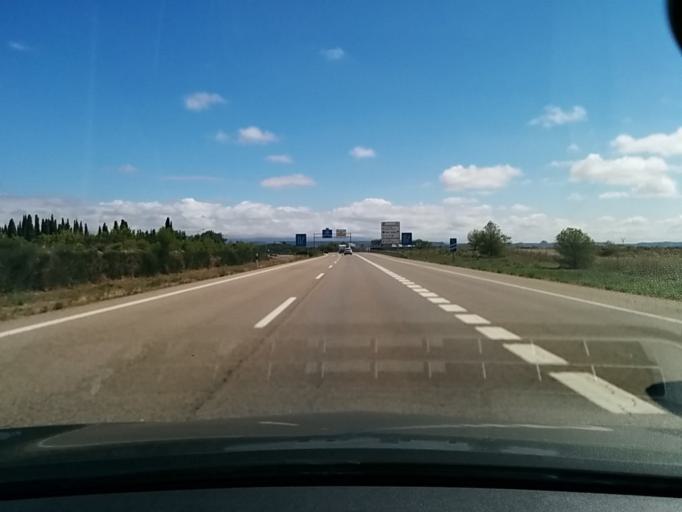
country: ES
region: Aragon
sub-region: Provincia de Huesca
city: Huesca
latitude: 42.1200
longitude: -0.4363
